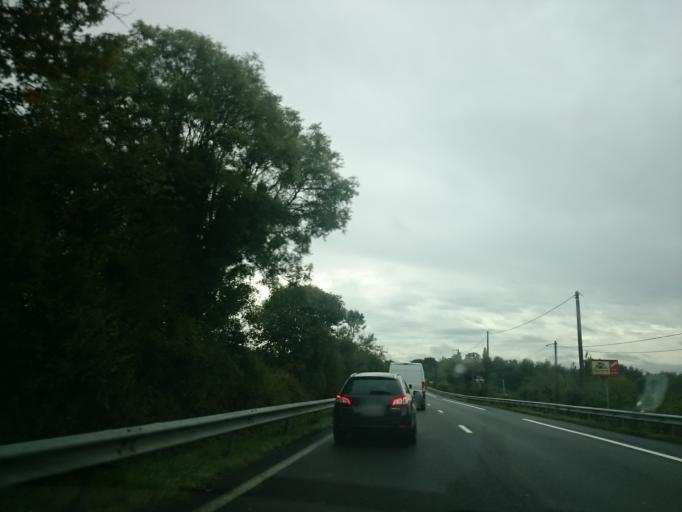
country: FR
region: Pays de la Loire
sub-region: Departement de la Loire-Atlantique
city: Vigneux-de-Bretagne
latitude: 47.2932
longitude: -1.7447
